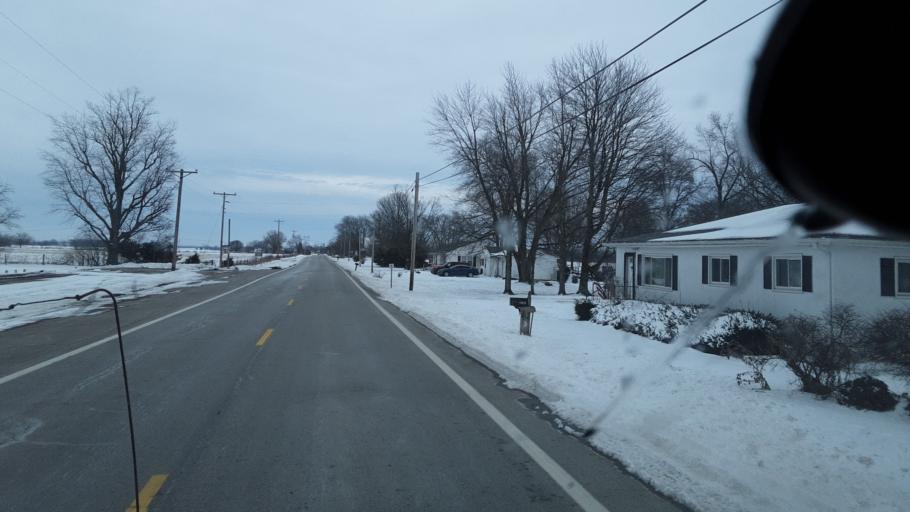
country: US
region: Ohio
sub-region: Madison County
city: Mount Sterling
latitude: 39.6736
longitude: -83.1769
